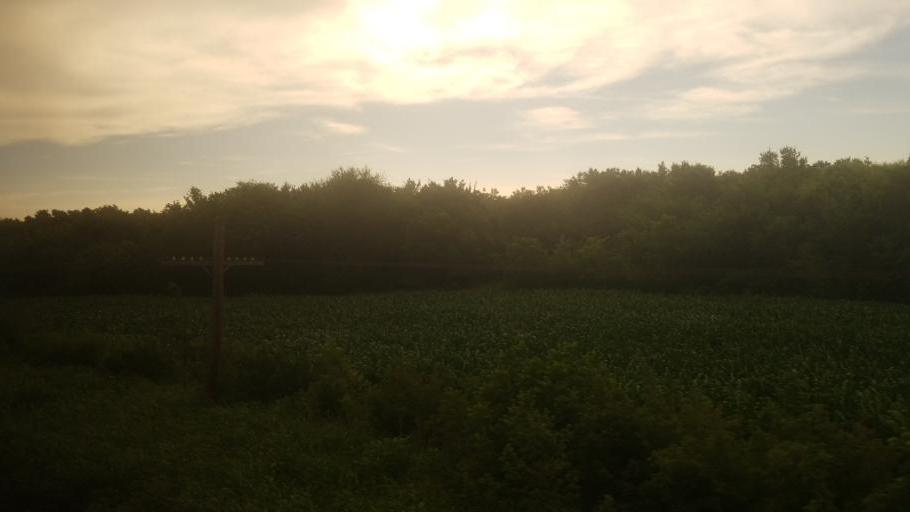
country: US
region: Kansas
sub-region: Osage County
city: Carbondale
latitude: 38.9213
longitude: -95.6947
